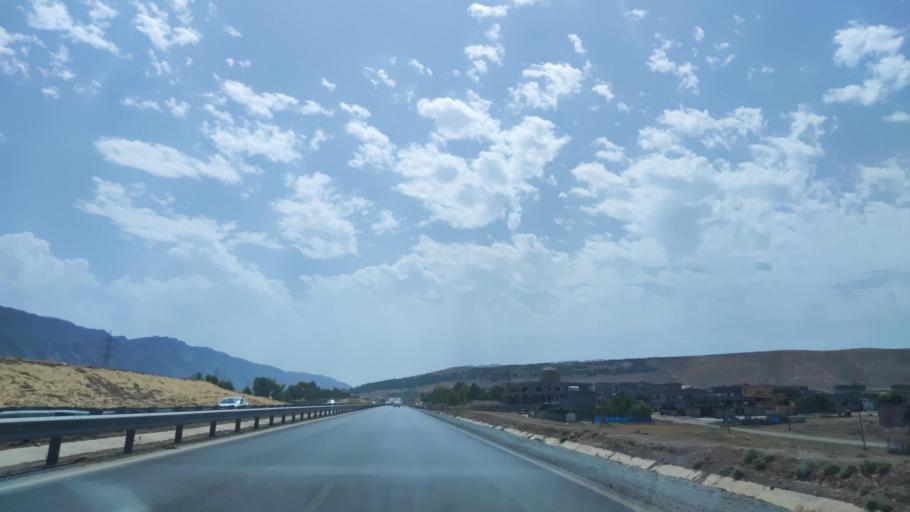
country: IQ
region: Arbil
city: Shaqlawah
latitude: 36.5042
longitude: 44.3530
